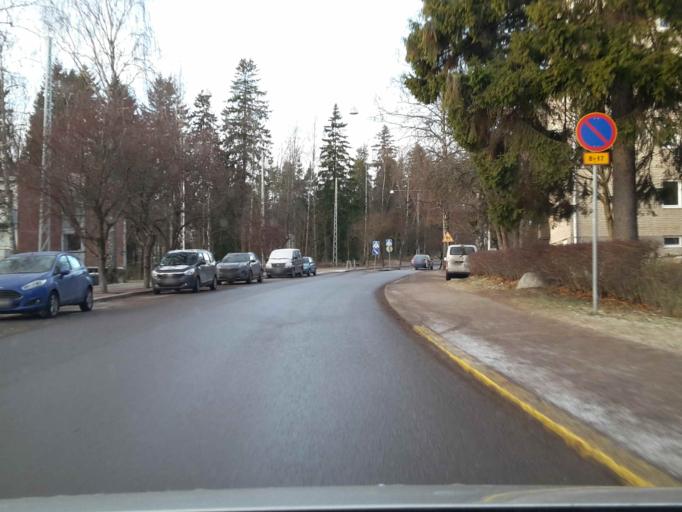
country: FI
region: Uusimaa
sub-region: Helsinki
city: Teekkarikylae
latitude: 60.1569
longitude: 24.8643
